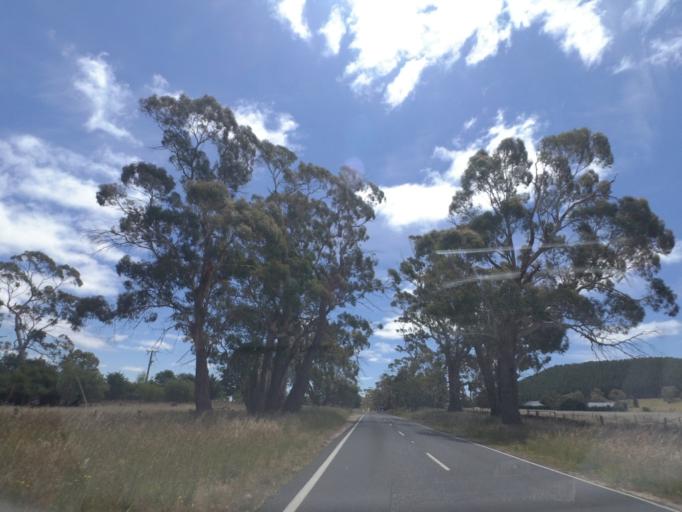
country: AU
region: Victoria
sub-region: Mount Alexander
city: Castlemaine
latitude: -37.2757
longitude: 144.1479
